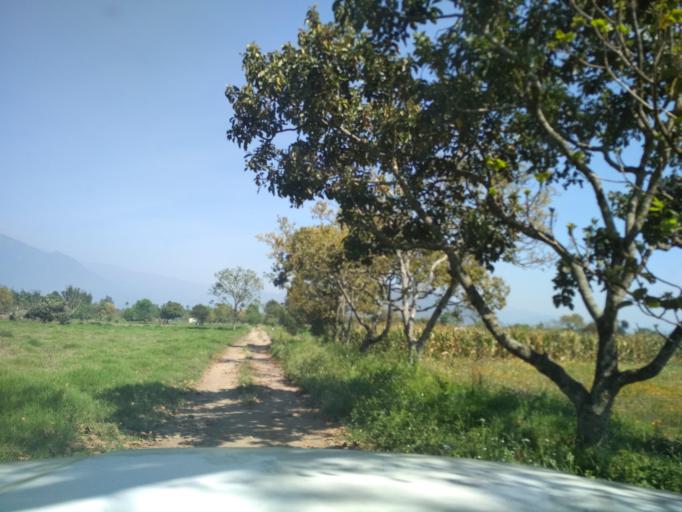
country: MX
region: Veracruz
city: Jalapilla
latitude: 18.8123
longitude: -97.0840
